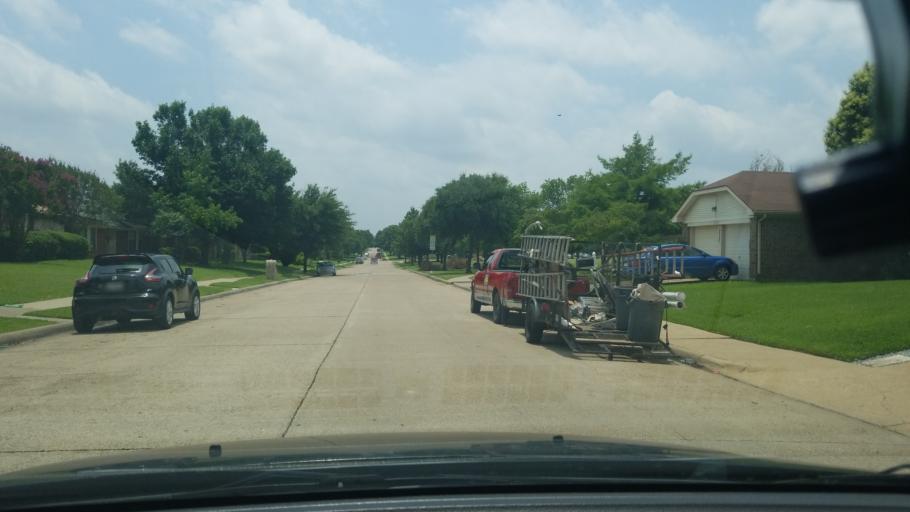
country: US
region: Texas
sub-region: Dallas County
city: Mesquite
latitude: 32.8045
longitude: -96.6155
